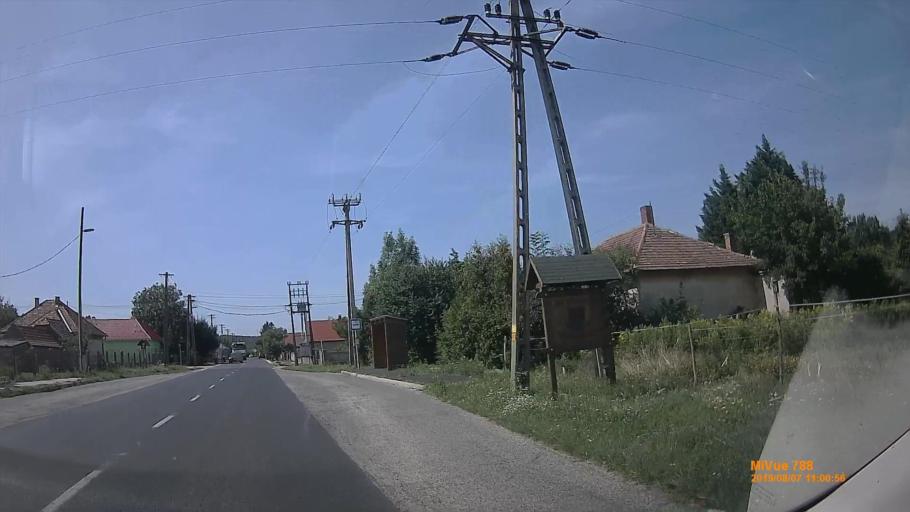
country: HU
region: Veszprem
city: Ajka
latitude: 47.0377
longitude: 17.5386
